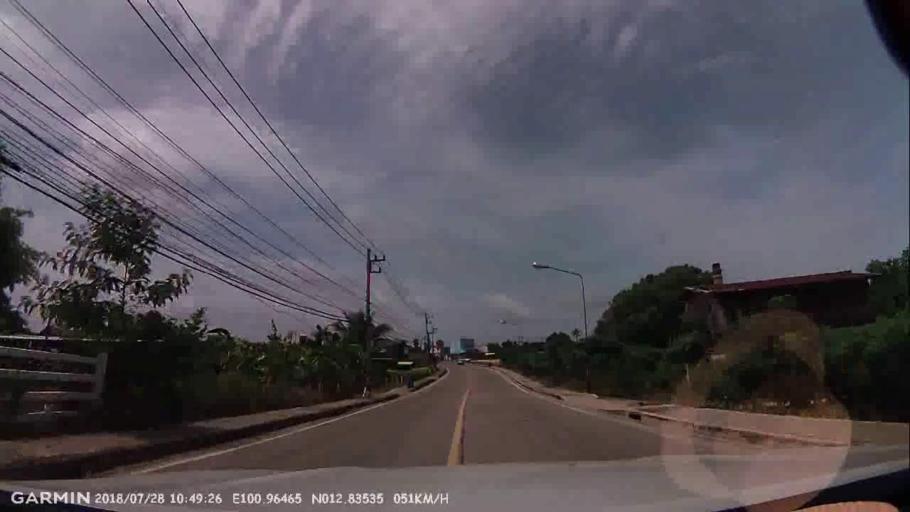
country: TH
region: Chon Buri
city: Phatthaya
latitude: 12.8352
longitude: 100.9646
